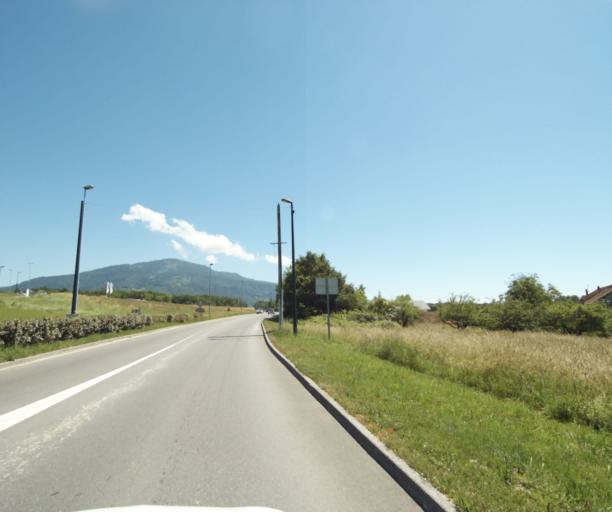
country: FR
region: Rhone-Alpes
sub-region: Departement de la Haute-Savoie
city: Loisin
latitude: 46.2704
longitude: 6.3133
